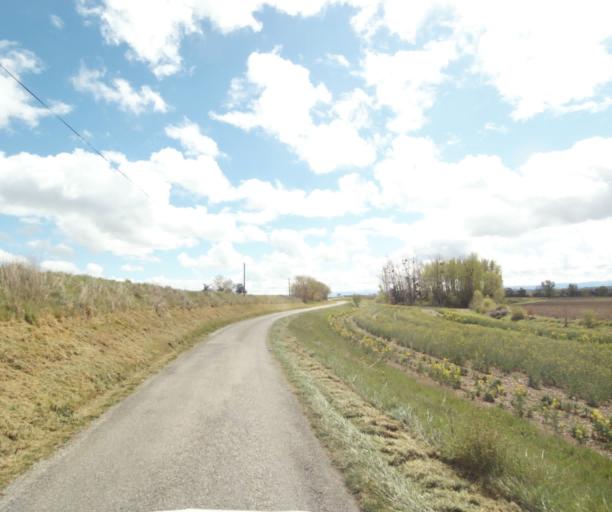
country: FR
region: Midi-Pyrenees
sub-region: Departement de l'Ariege
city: Saverdun
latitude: 43.2670
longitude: 1.5832
